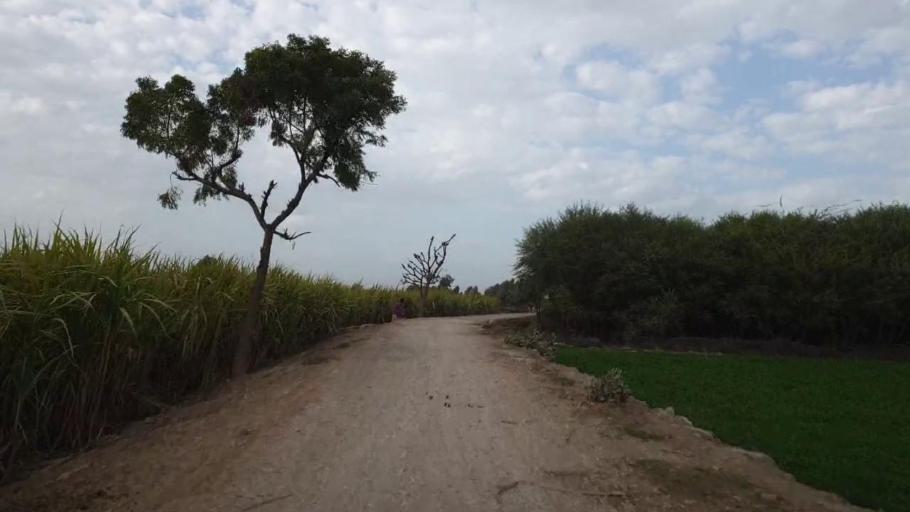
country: PK
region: Sindh
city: Tando Adam
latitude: 25.6566
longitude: 68.6116
